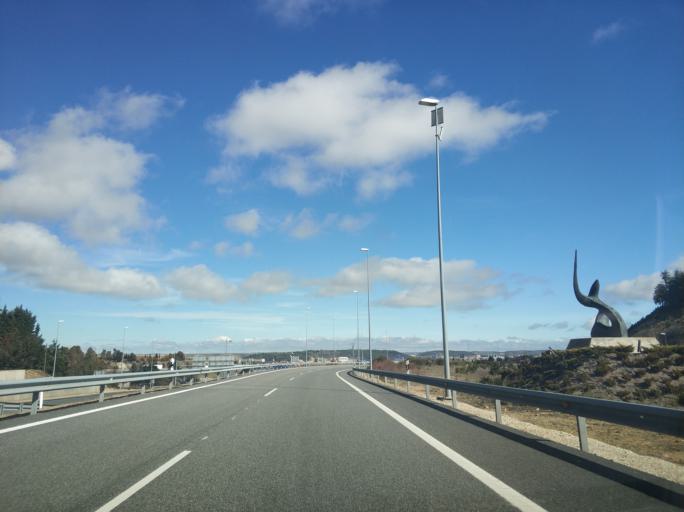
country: ES
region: Castille and Leon
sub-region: Provincia de Burgos
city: Villagonzalo-Pedernales
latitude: 42.3118
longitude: -3.7025
